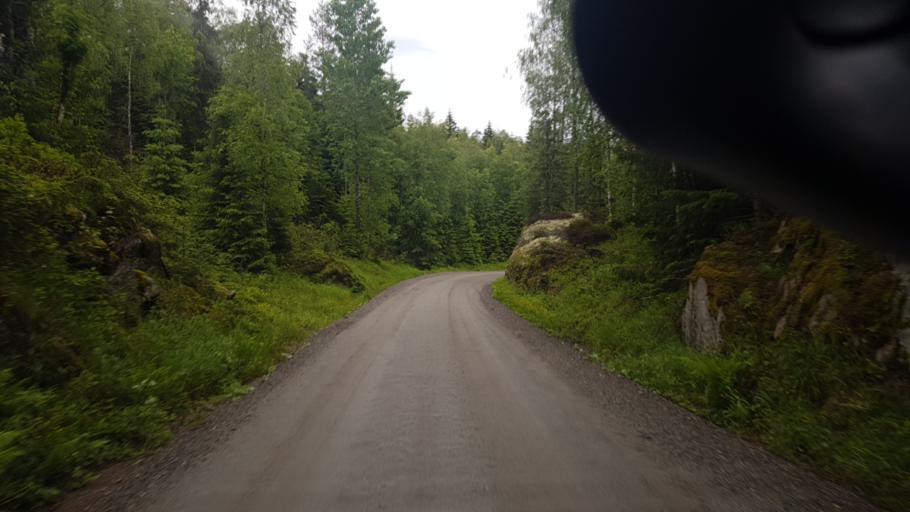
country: NO
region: Ostfold
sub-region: Romskog
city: Romskog
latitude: 59.7148
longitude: 11.9861
